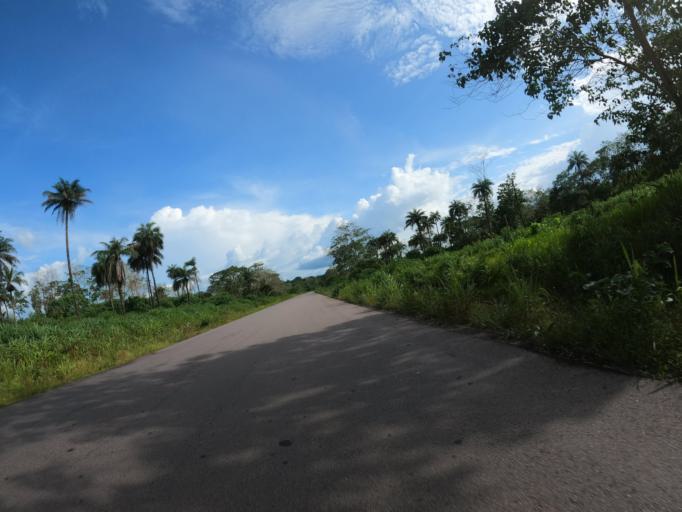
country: SL
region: Northern Province
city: Makeni
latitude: 9.0411
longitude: -12.1718
